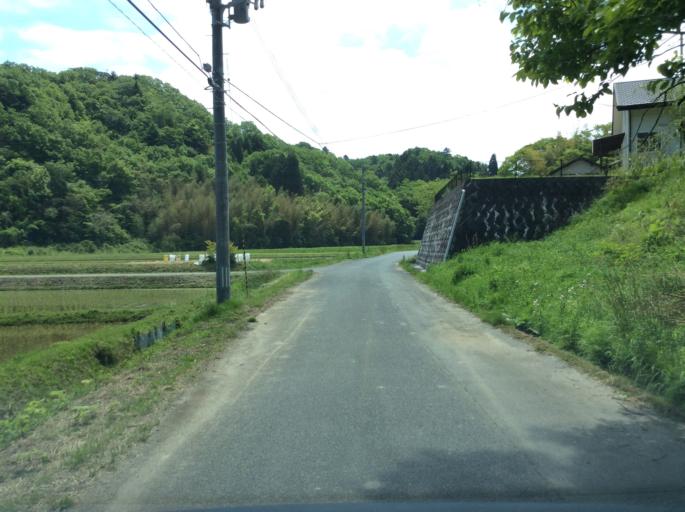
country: JP
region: Fukushima
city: Iwaki
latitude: 37.0092
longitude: 140.9457
